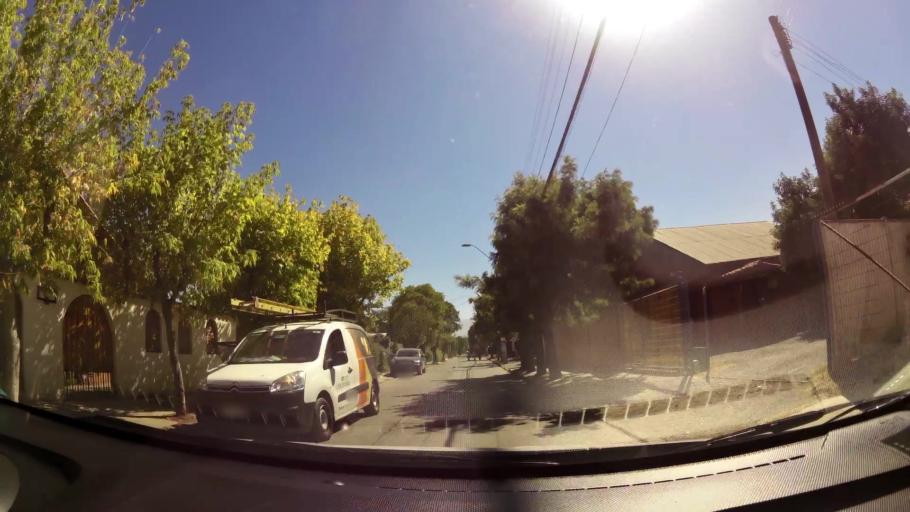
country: CL
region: O'Higgins
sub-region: Provincia de Cachapoal
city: Rancagua
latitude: -34.1724
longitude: -70.7030
